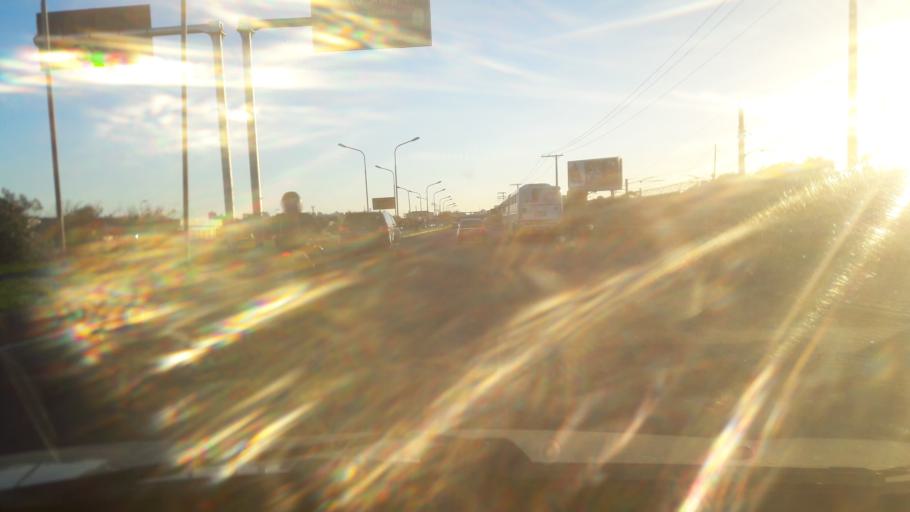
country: BR
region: Rio Grande do Sul
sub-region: Porto Alegre
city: Porto Alegre
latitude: -29.9917
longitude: -51.1855
